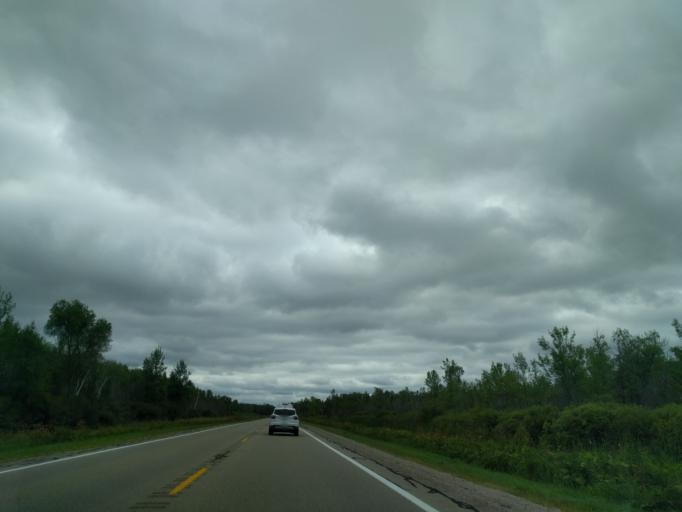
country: US
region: Michigan
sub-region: Menominee County
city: Menominee
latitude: 45.3367
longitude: -87.4179
